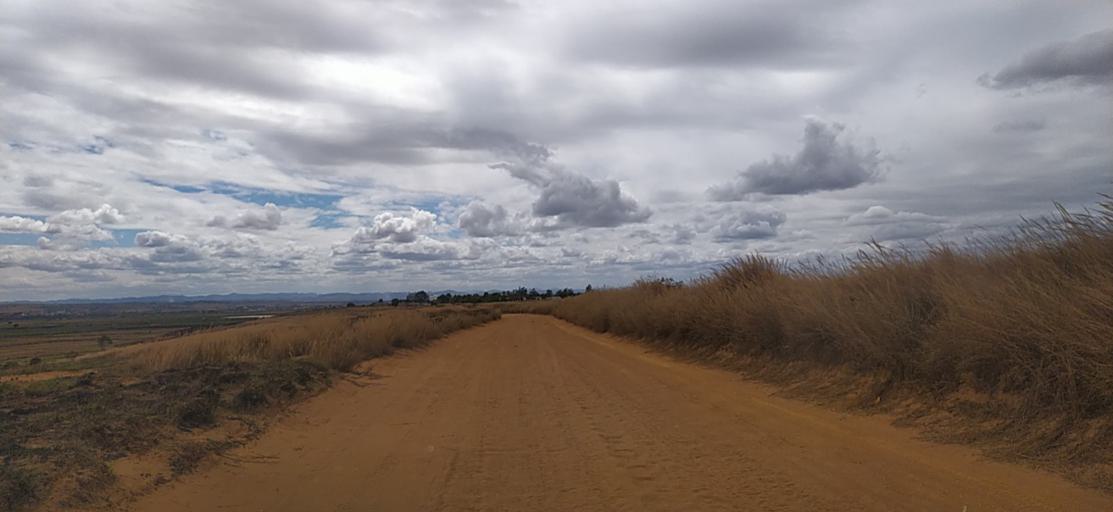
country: MG
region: Alaotra Mangoro
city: Ambatondrazaka
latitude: -17.9059
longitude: 48.2607
